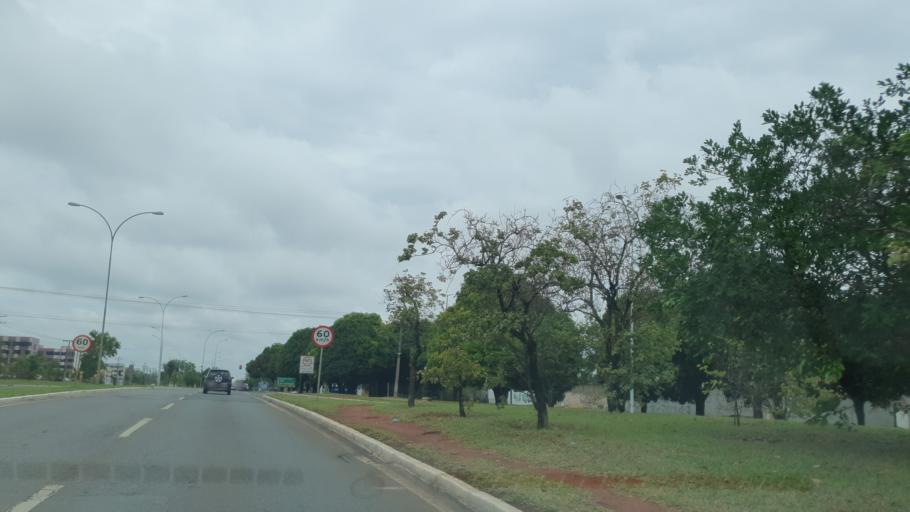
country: BR
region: Federal District
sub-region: Brasilia
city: Brasilia
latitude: -15.7815
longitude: -47.9298
